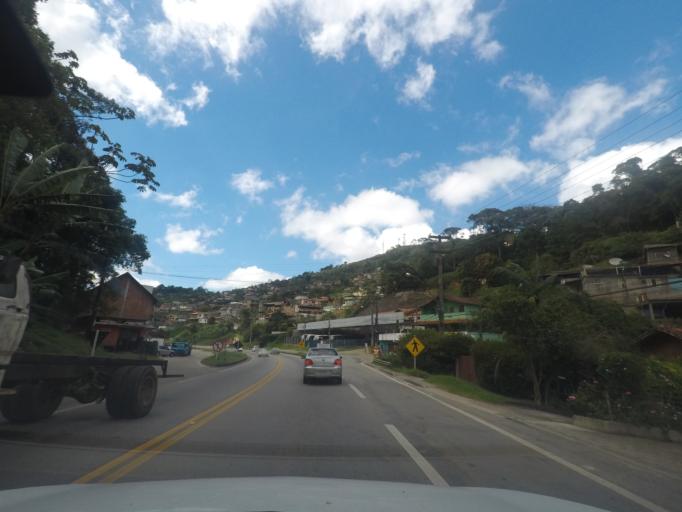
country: BR
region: Rio de Janeiro
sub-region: Teresopolis
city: Teresopolis
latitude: -22.3980
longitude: -42.9550
